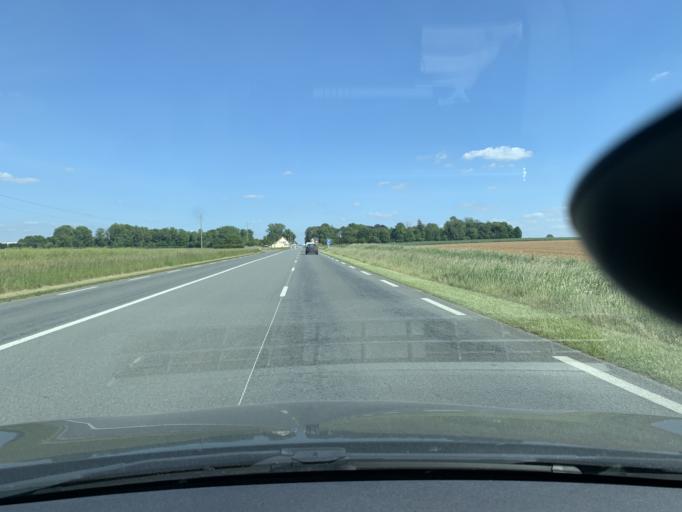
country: FR
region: Nord-Pas-de-Calais
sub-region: Departement du Nord
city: Fontaine-au-Pire
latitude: 50.1519
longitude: 3.3344
